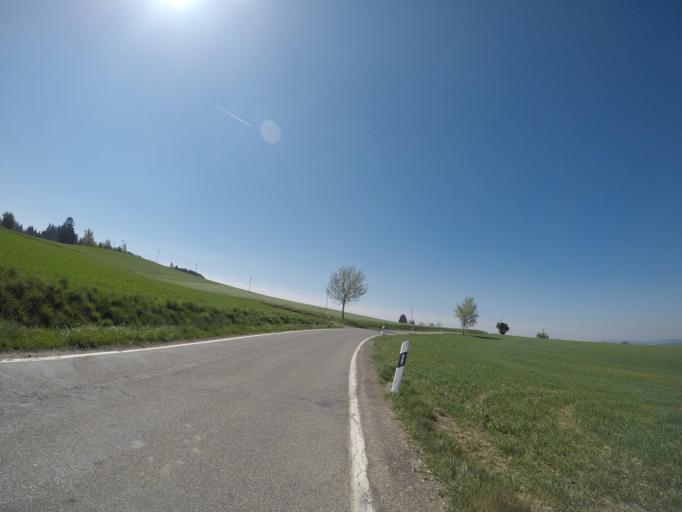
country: DE
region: Baden-Wuerttemberg
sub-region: Tuebingen Region
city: Markdorf
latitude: 47.7522
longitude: 9.3945
